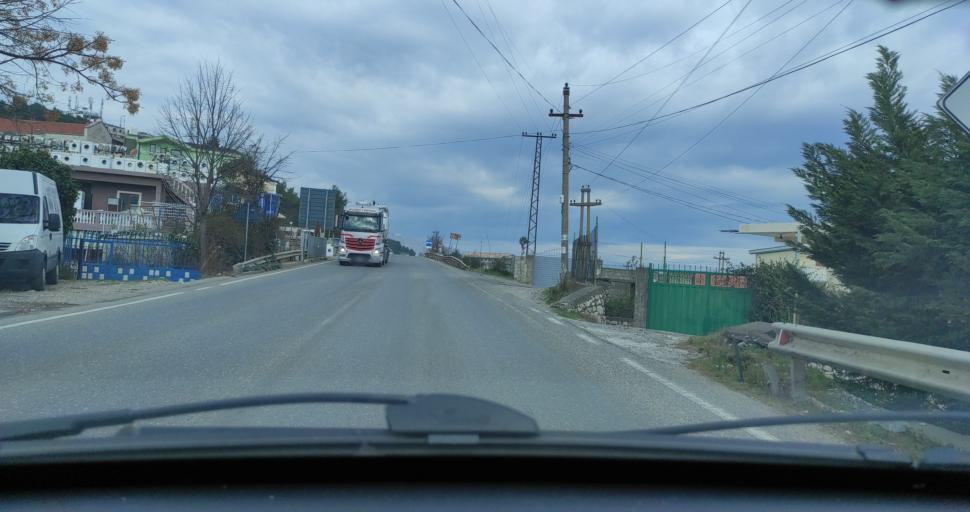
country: AL
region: Lezhe
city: Lezhe
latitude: 41.7843
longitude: 19.6405
